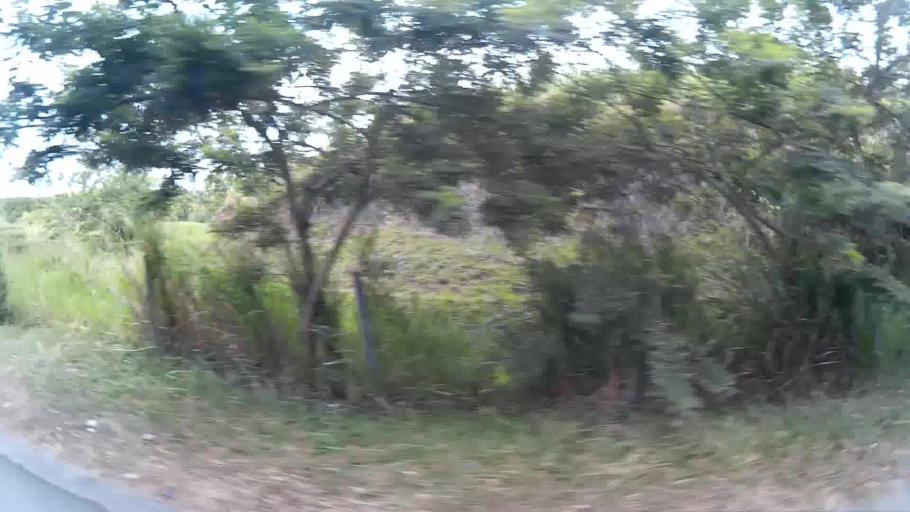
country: CO
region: Risaralda
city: La Virginia
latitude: 4.8393
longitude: -75.8582
